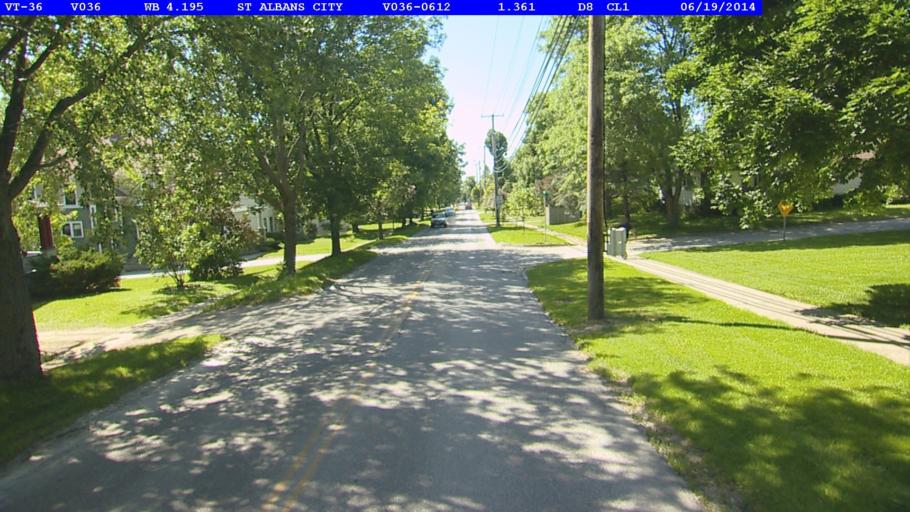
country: US
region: Vermont
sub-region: Franklin County
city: Saint Albans
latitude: 44.8072
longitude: -73.0744
